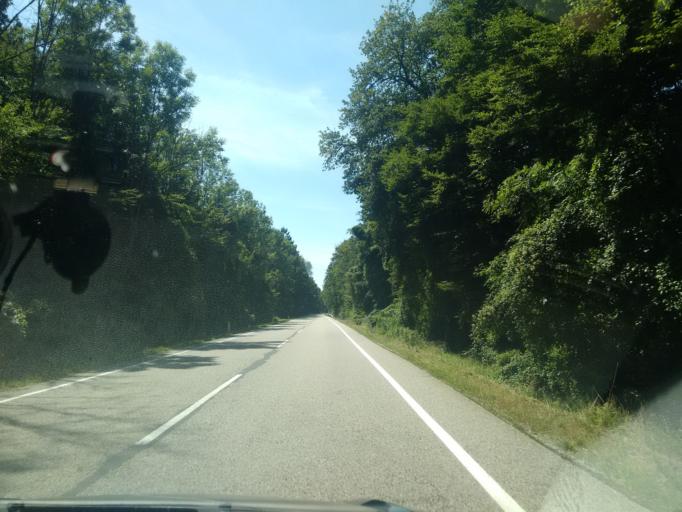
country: DE
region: Bavaria
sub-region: Upper Bavaria
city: Haiming
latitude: 48.2012
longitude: 12.9040
